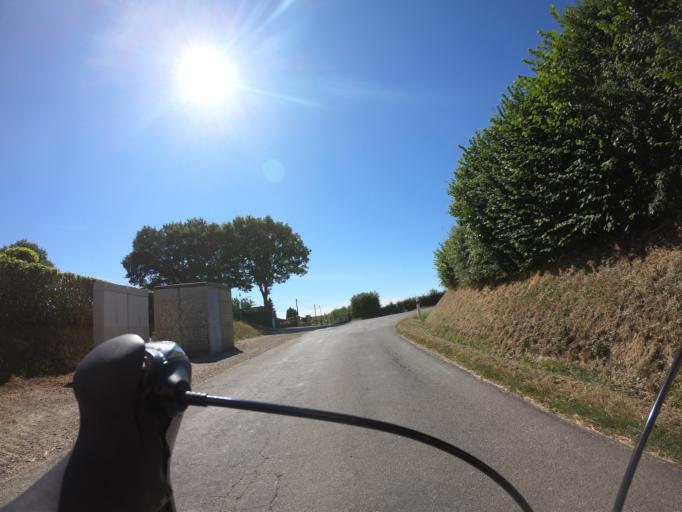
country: FR
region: Lower Normandy
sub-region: Departement de l'Orne
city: Saint-Denis-sur-Sarthon
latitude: 48.5164
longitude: -0.0823
